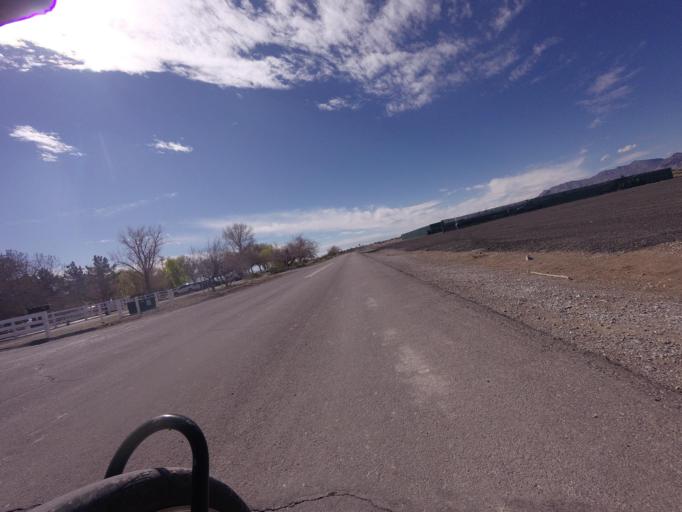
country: US
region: Nevada
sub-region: Clark County
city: North Las Vegas
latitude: 36.3216
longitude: -115.2700
